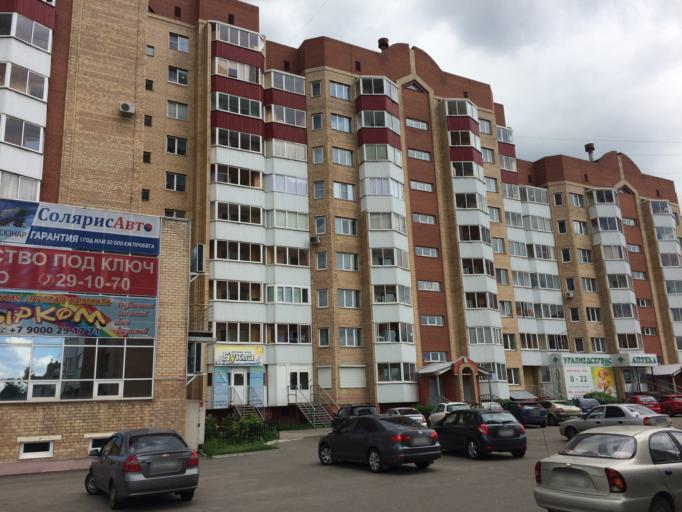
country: RU
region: Chelyabinsk
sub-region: Gorod Magnitogorsk
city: Magnitogorsk
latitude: 53.3640
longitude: 58.9504
